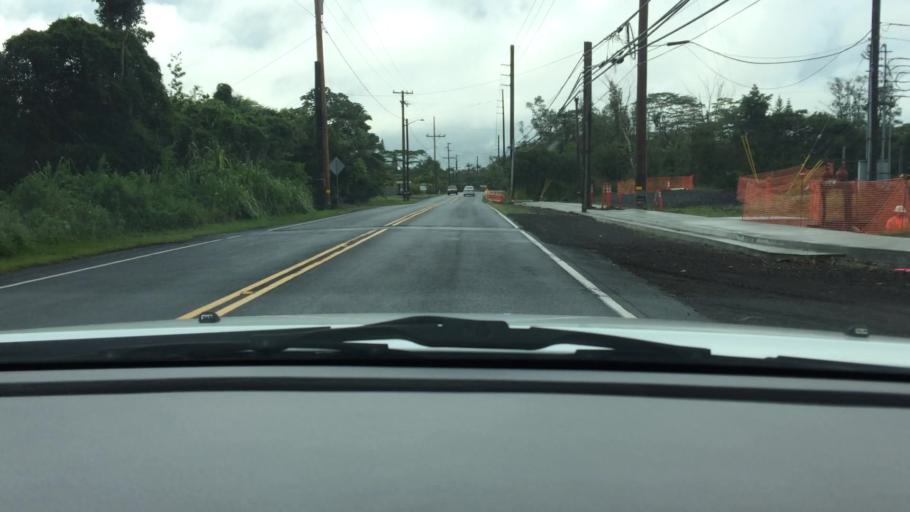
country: US
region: Hawaii
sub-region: Hawaii County
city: Hawaiian Paradise Park
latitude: 19.5029
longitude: -154.9553
